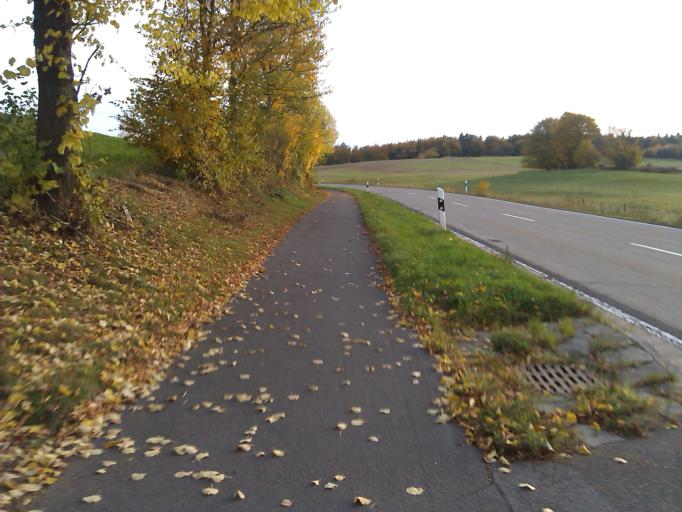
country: DE
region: Rheinland-Pfalz
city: Schneckenhausen
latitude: 49.5313
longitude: 7.7486
